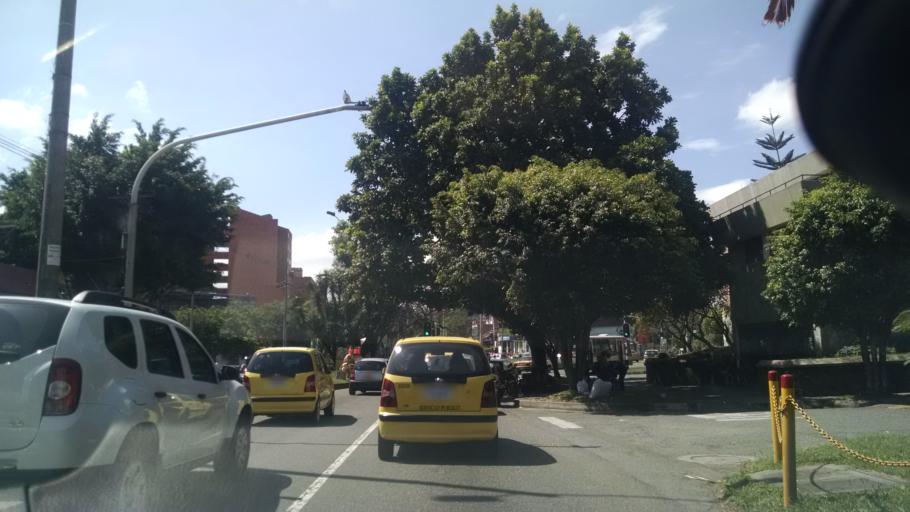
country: CO
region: Antioquia
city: Medellin
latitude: 6.2395
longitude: -75.6030
